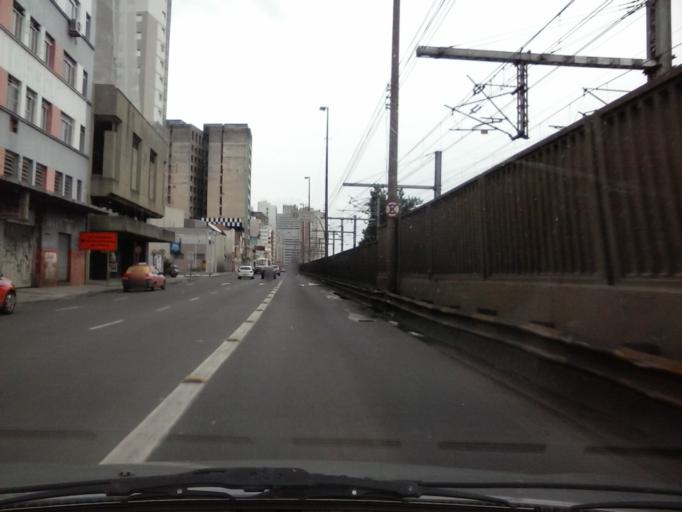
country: BR
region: Rio Grande do Sul
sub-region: Porto Alegre
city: Porto Alegre
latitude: -30.0233
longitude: -51.2213
